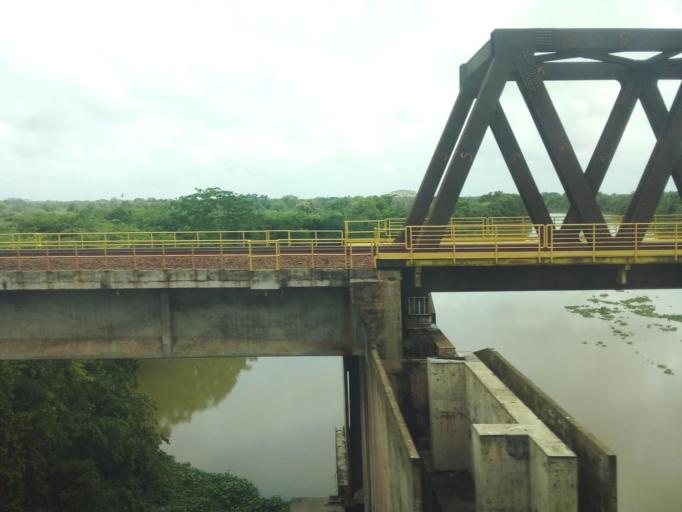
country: BR
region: Maranhao
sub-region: Vitoria Do Mearim
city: Vitoria do Mearim
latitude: -3.5464
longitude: -44.8323
